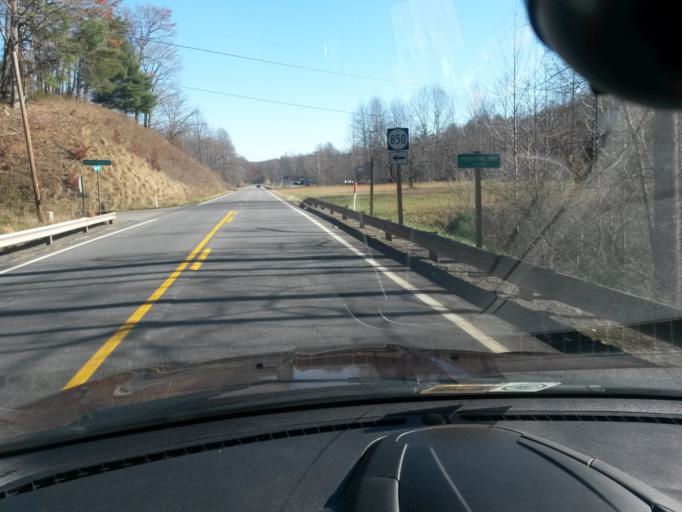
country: US
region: Virginia
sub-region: Patrick County
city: Patrick Springs
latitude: 36.7537
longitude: -80.1911
